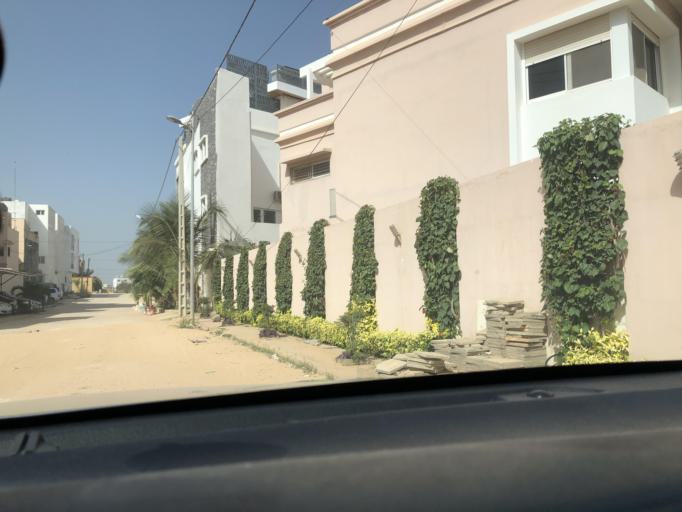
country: SN
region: Dakar
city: Mermoz Boabab
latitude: 14.7322
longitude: -17.5004
